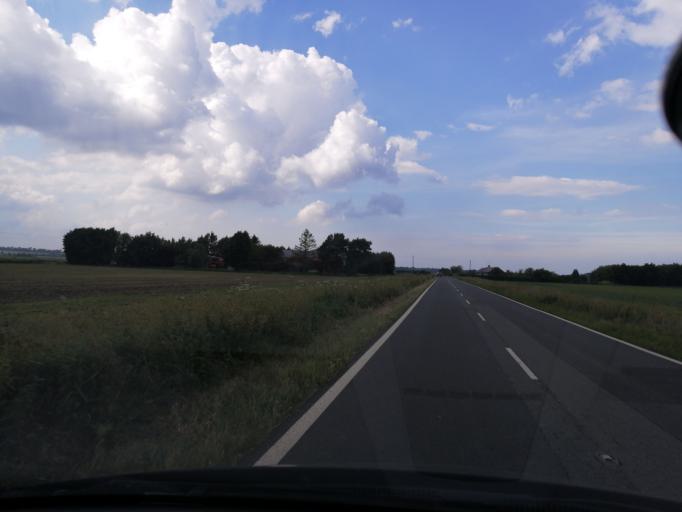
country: GB
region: England
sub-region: Cambridgeshire
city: Yaxley
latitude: 52.4914
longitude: -0.2435
